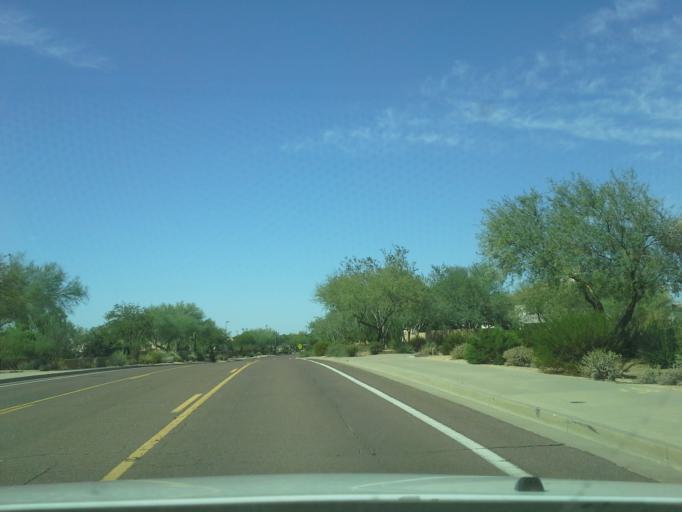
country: US
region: Arizona
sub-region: Maricopa County
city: Carefree
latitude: 33.6773
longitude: -111.9140
